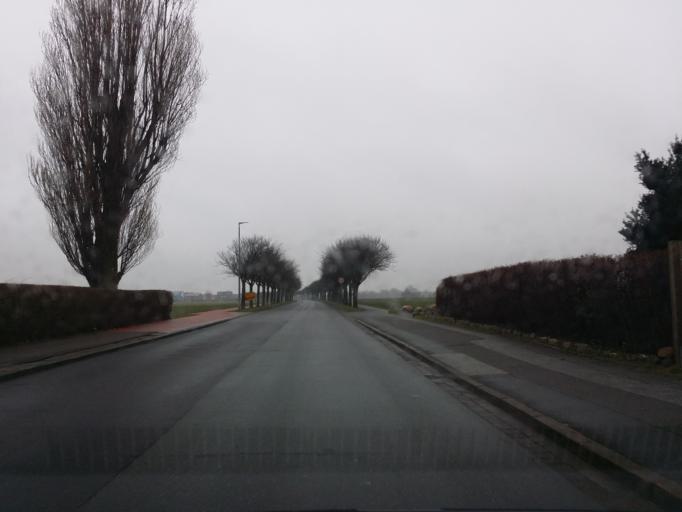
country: DE
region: Schleswig-Holstein
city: Burg auf Fehmarn
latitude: 54.4234
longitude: 11.2066
